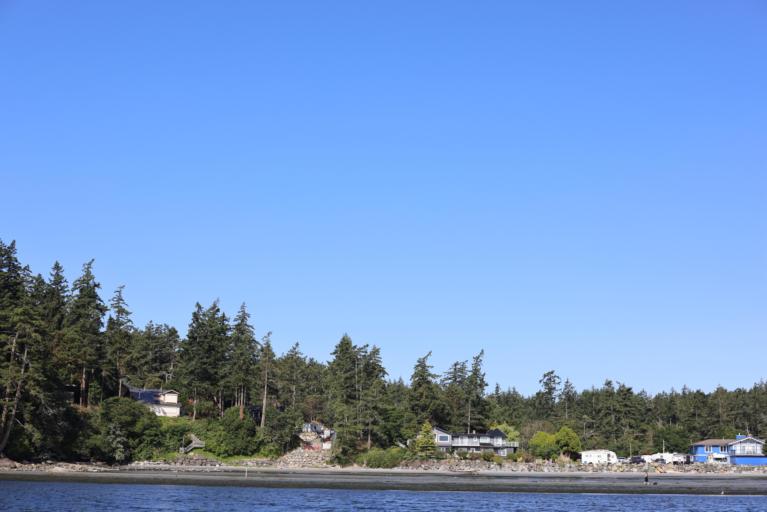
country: CA
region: British Columbia
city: Metchosin
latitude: 48.3514
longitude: -123.5417
